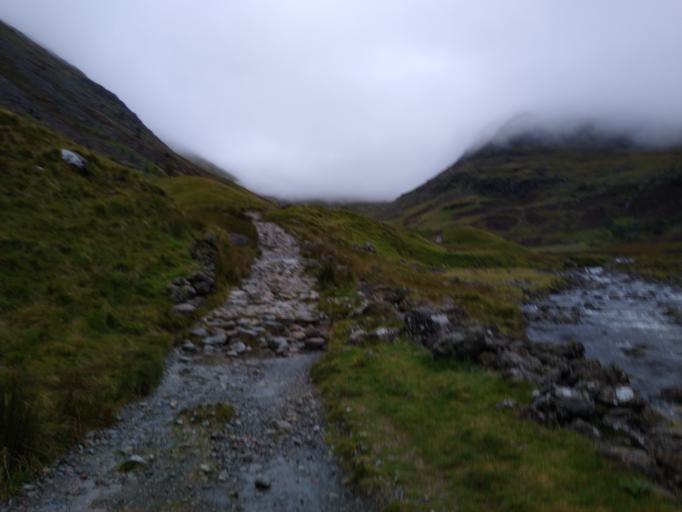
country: GB
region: England
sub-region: Cumbria
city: Keswick
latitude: 54.4933
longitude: -3.1824
